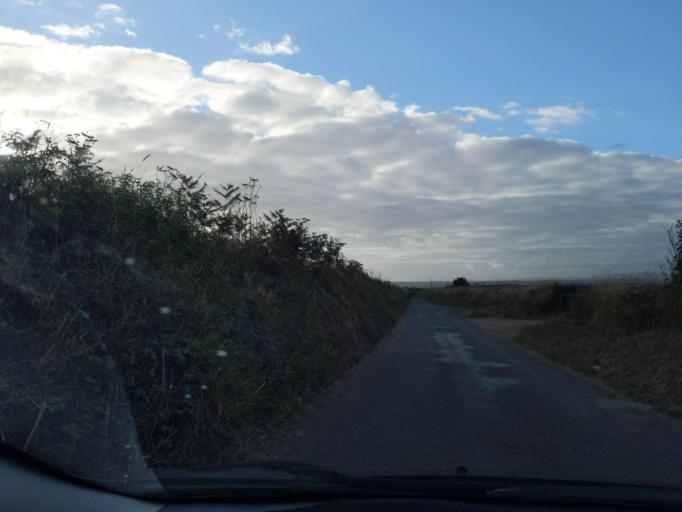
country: GB
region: England
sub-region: Devon
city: Salcombe
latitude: 50.2329
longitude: -3.8167
